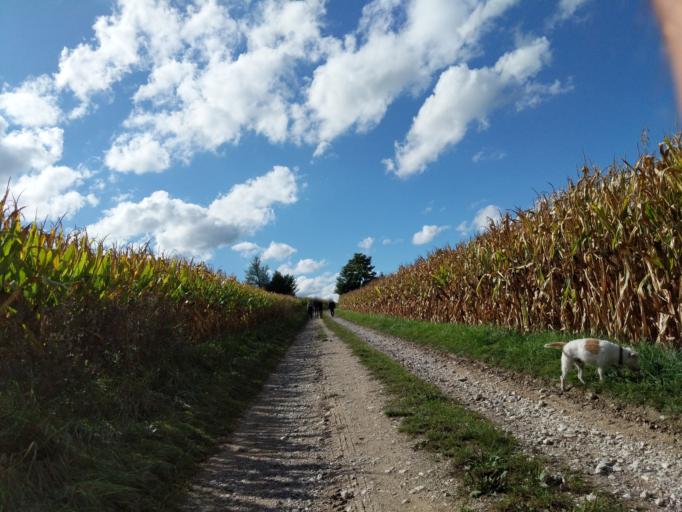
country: DE
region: Bavaria
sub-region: Lower Bavaria
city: Bad Abbach
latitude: 48.9464
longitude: 12.0609
